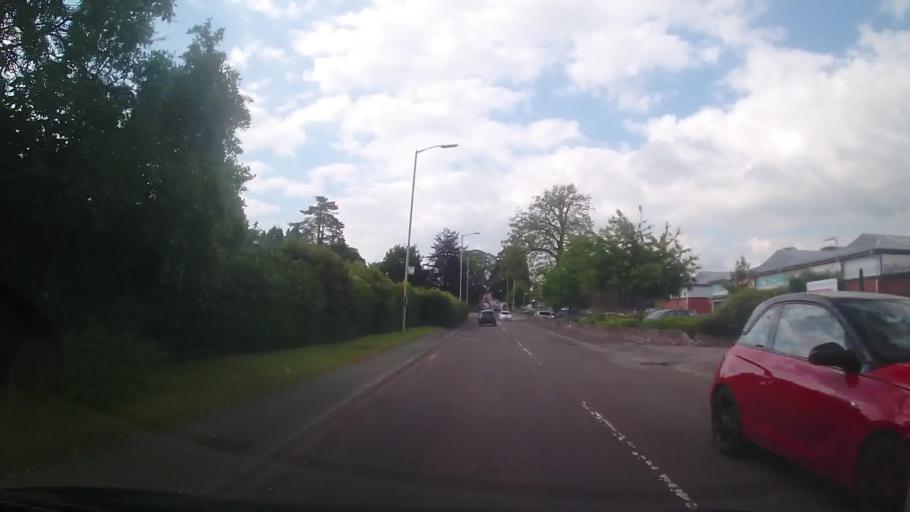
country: GB
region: England
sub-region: Shropshire
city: Oswestry
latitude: 52.8548
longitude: -3.0488
